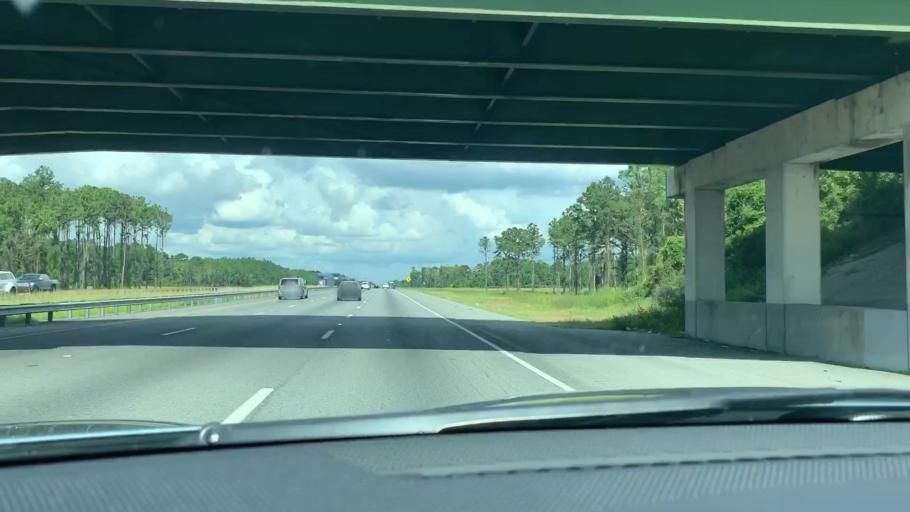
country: US
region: Georgia
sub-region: Glynn County
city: Brunswick
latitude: 31.1018
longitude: -81.5978
